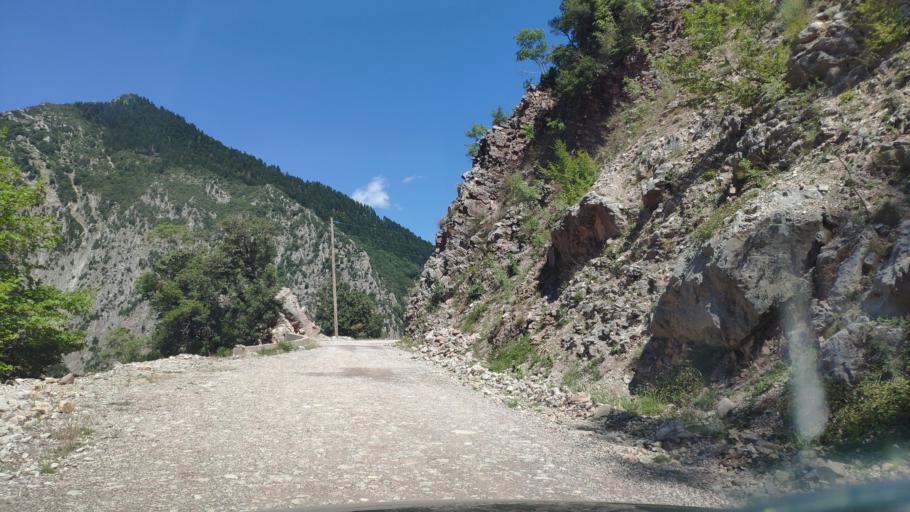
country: GR
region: Central Greece
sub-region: Nomos Evrytanias
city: Kerasochori
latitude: 39.1117
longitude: 21.6160
